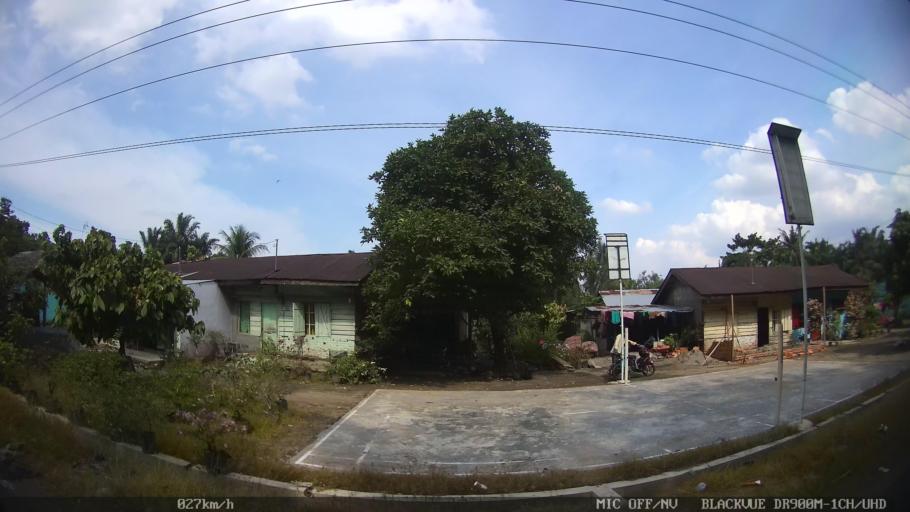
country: ID
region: North Sumatra
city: Binjai
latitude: 3.6490
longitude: 98.5180
